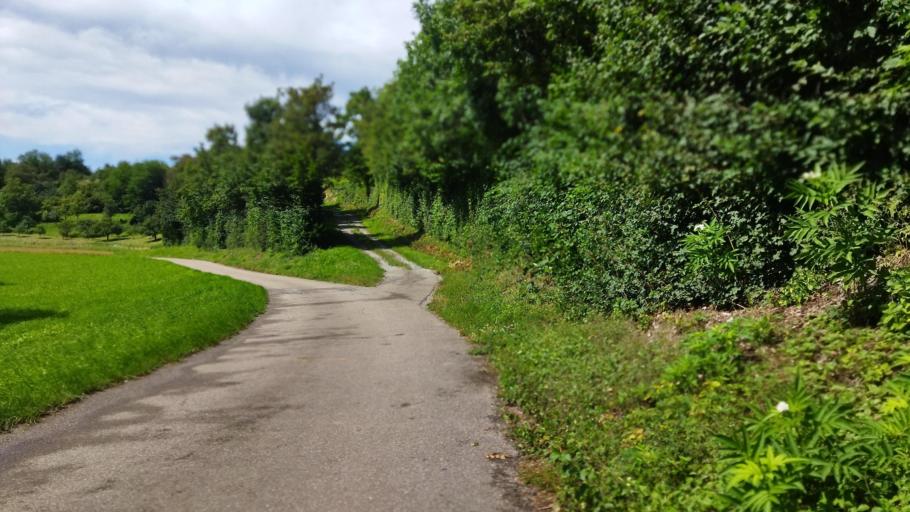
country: DE
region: Baden-Wuerttemberg
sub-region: Regierungsbezirk Stuttgart
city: Besigheim
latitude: 49.0112
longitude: 9.1369
